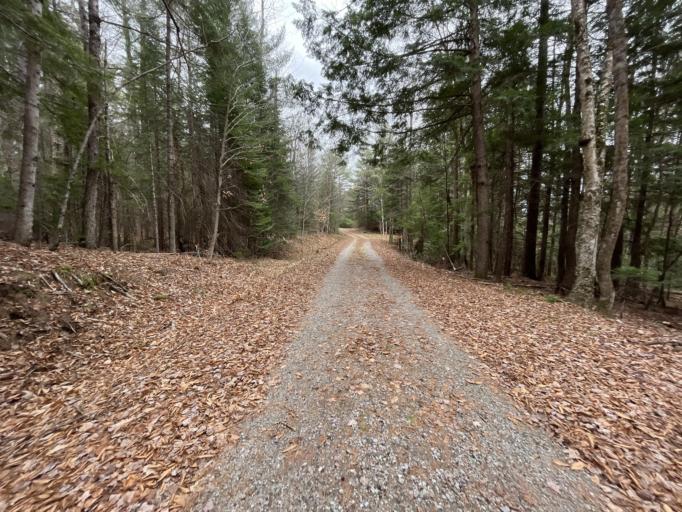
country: US
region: New Hampshire
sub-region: Merrimack County
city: New London
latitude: 43.4060
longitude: -71.9833
